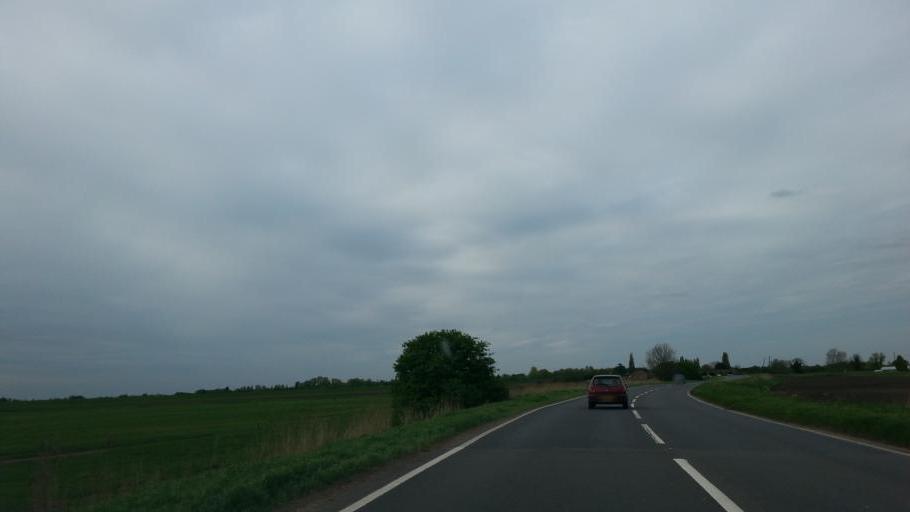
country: GB
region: England
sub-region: Cambridgeshire
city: March
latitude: 52.5962
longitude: 0.0604
